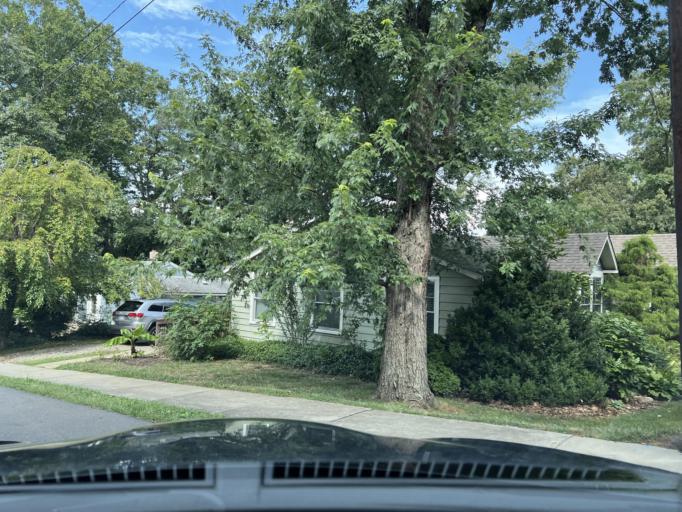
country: US
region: North Carolina
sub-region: Buncombe County
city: Asheville
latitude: 35.5716
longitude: -82.5415
